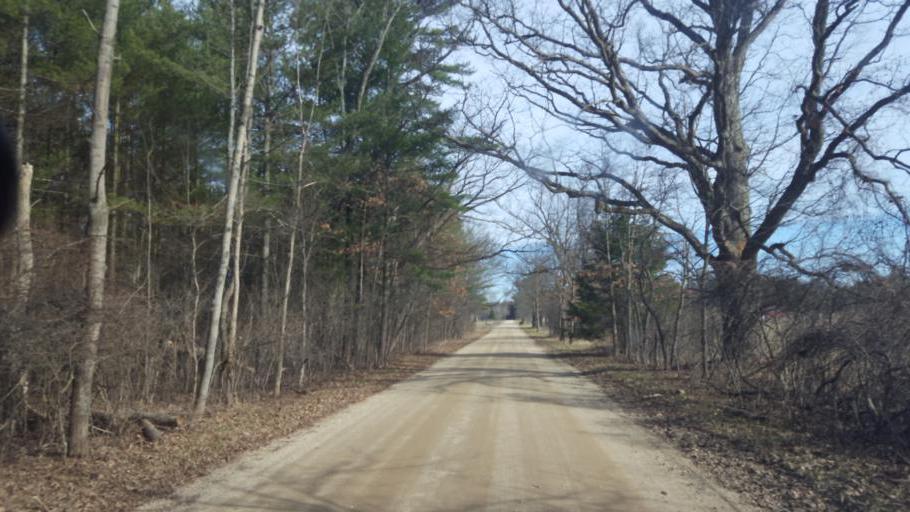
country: US
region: Michigan
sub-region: Montcalm County
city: Howard City
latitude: 43.5354
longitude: -85.5625
